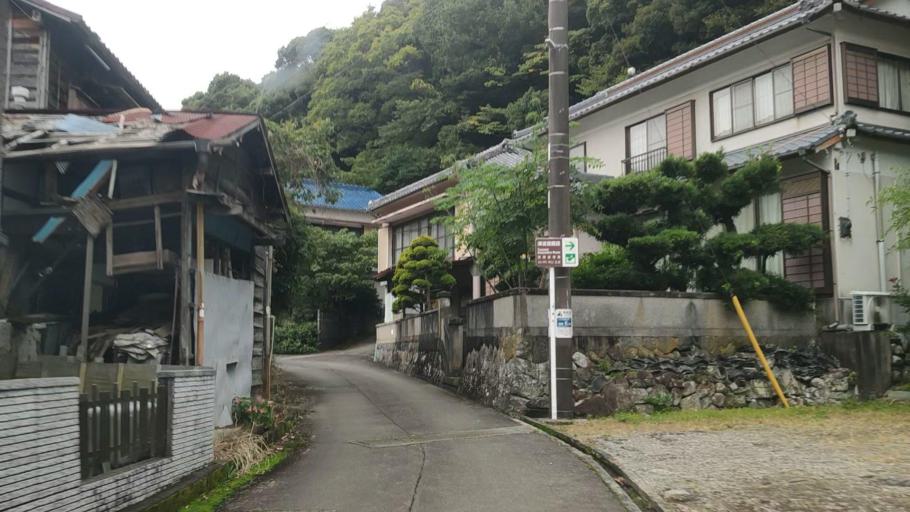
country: JP
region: Shizuoka
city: Heda
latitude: 35.0133
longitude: 138.8432
